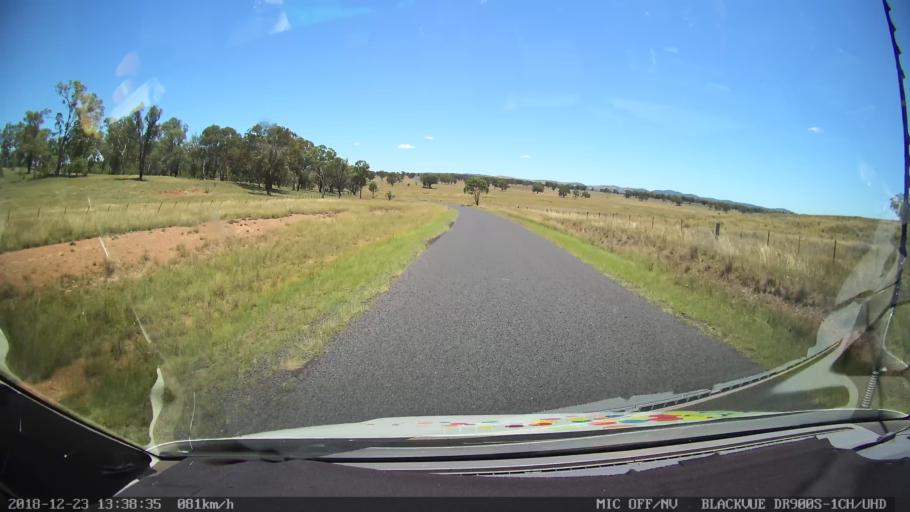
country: AU
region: New South Wales
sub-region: Armidale Dumaresq
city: Armidale
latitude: -30.4512
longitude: 151.2109
